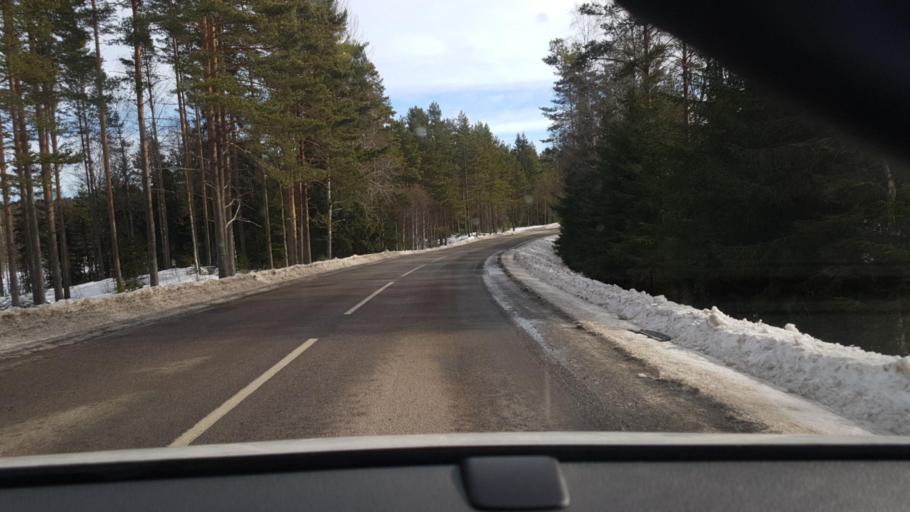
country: SE
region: Vaermland
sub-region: Arjangs Kommun
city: Arjaeng
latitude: 59.5651
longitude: 12.1871
